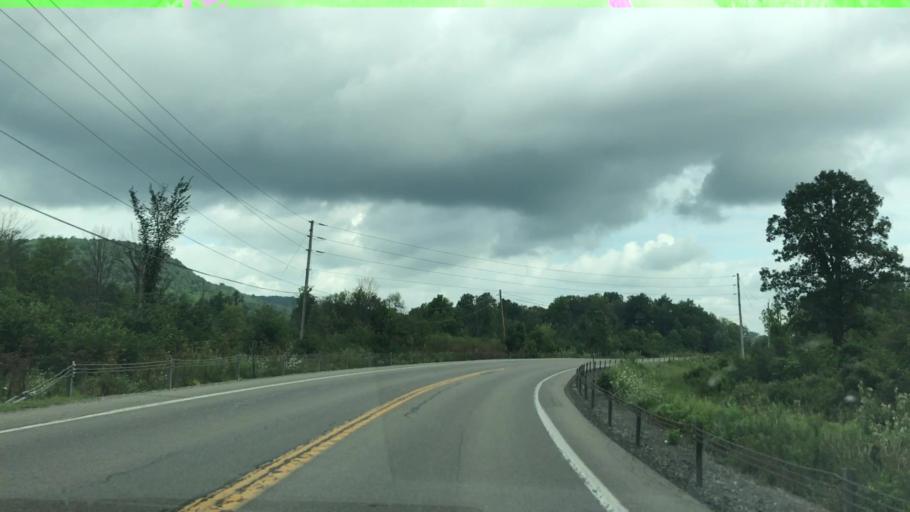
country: US
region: New York
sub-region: Steuben County
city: Bath
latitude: 42.4150
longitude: -77.3438
